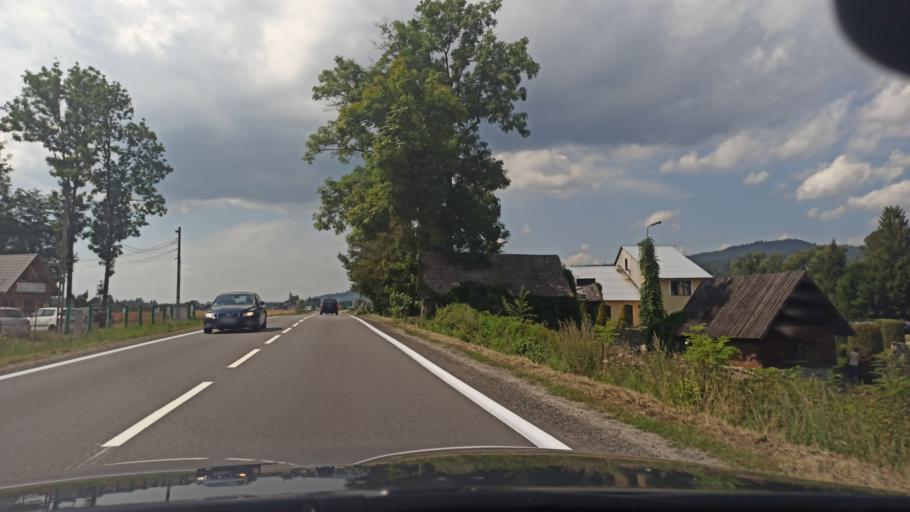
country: PL
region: Lesser Poland Voivodeship
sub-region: Powiat nowotarski
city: Frydman
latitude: 49.4719
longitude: 20.1877
